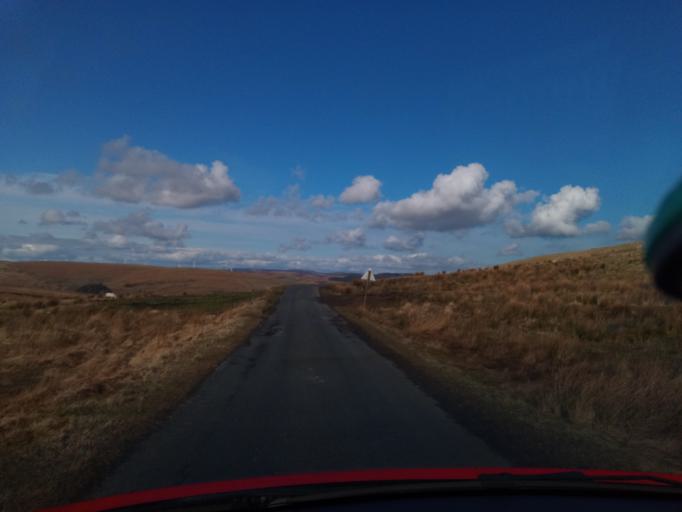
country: GB
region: Scotland
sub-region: The Scottish Borders
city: Hawick
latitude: 55.4423
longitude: -2.8855
